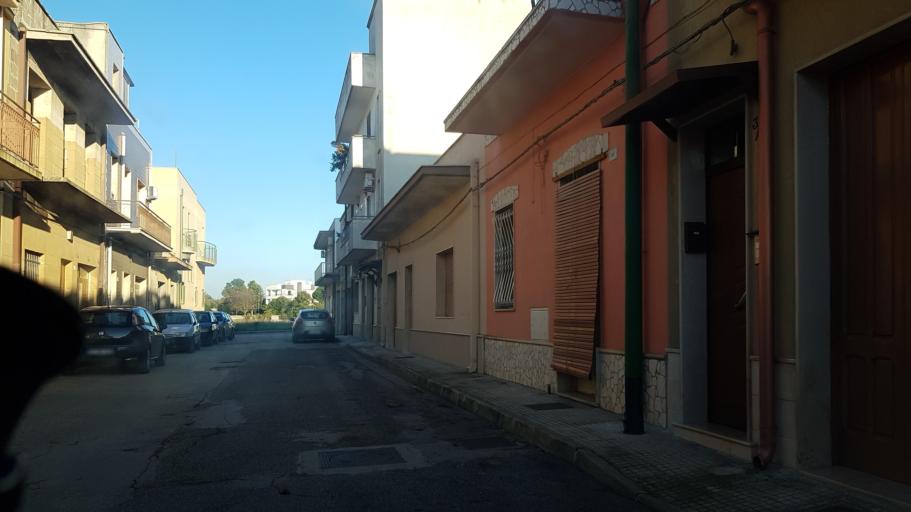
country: IT
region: Apulia
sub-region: Provincia di Brindisi
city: Latiano
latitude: 40.5488
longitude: 17.7212
